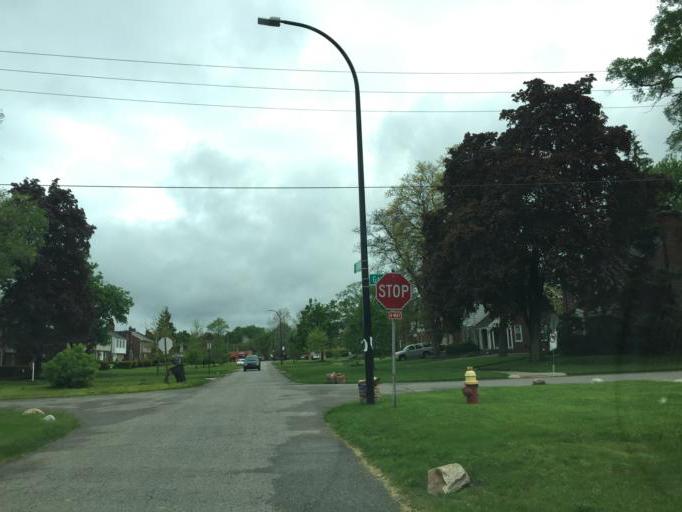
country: US
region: Michigan
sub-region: Oakland County
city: Southfield
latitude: 42.4134
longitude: -83.2228
